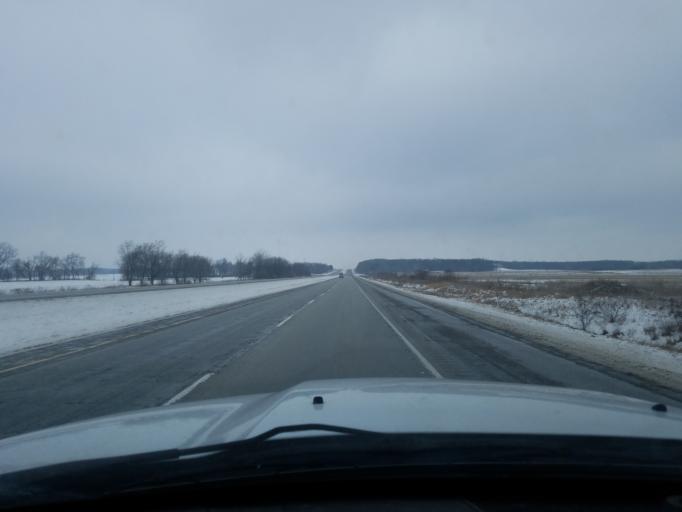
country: US
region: Indiana
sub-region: Fulton County
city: Rochester
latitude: 41.1020
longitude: -86.2398
